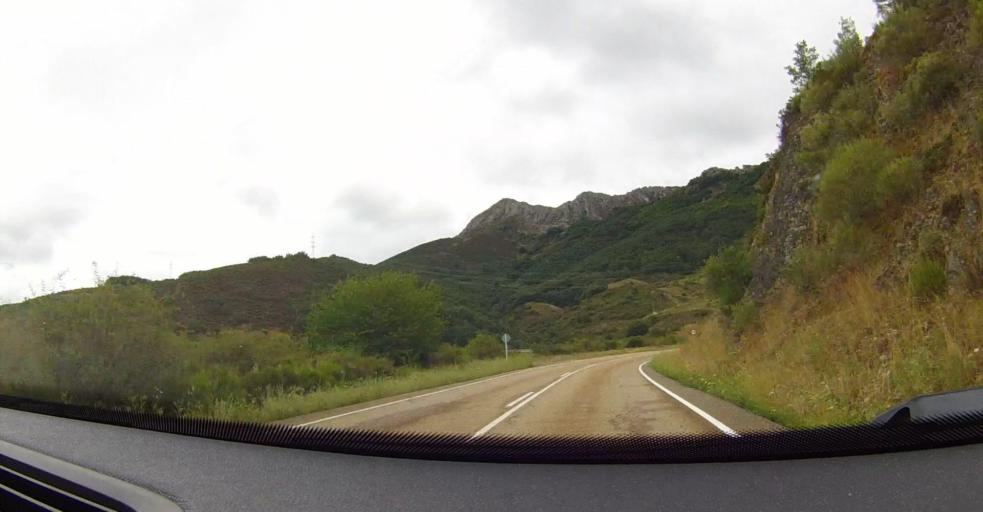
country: ES
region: Castille and Leon
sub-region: Provincia de Leon
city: Puebla de Lillo
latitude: 42.9348
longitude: -5.2759
